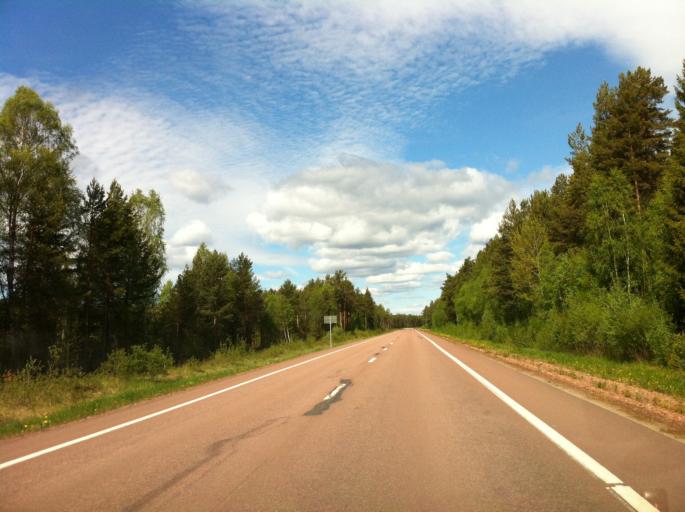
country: SE
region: Dalarna
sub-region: Mora Kommun
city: Mora
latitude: 60.9221
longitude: 14.5838
